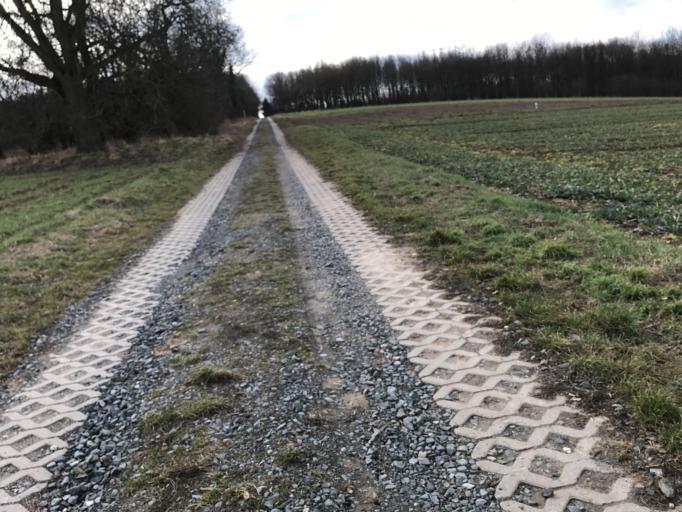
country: DE
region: Hesse
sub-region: Regierungsbezirk Darmstadt
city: Wiesbaden
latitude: 50.1031
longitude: 8.2840
